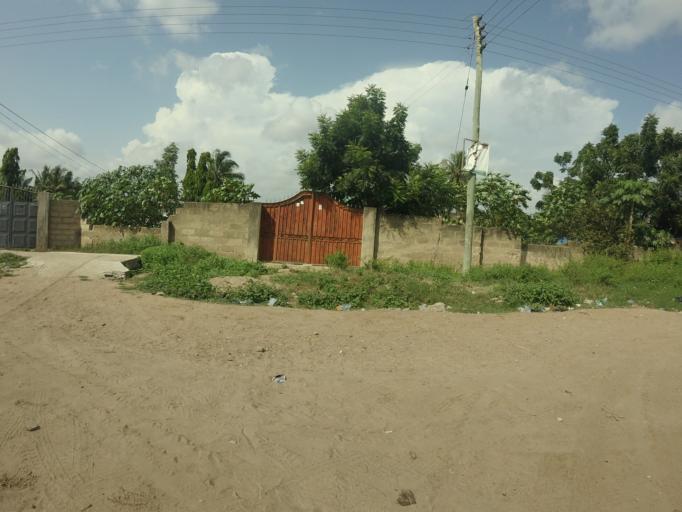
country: GH
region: Greater Accra
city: Dome
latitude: 5.6174
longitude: -0.2411
